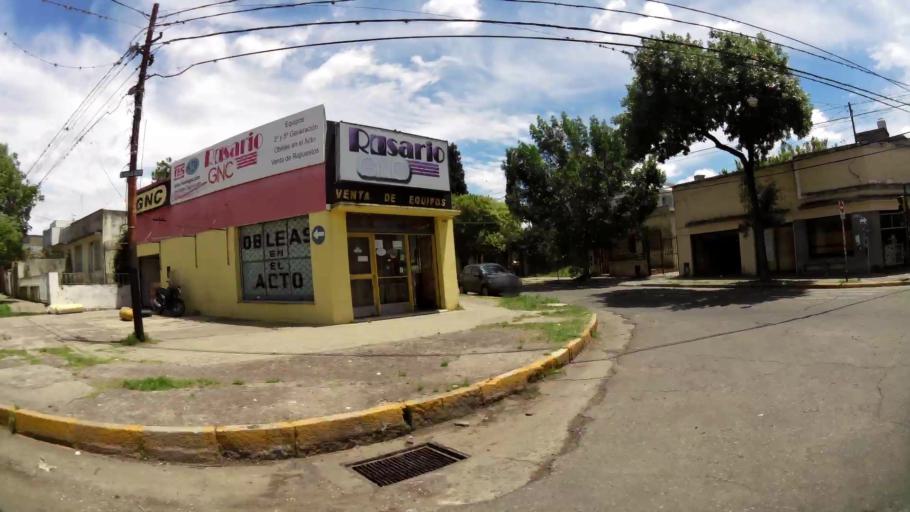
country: AR
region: Santa Fe
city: Gobernador Galvez
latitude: -32.9982
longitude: -60.6236
